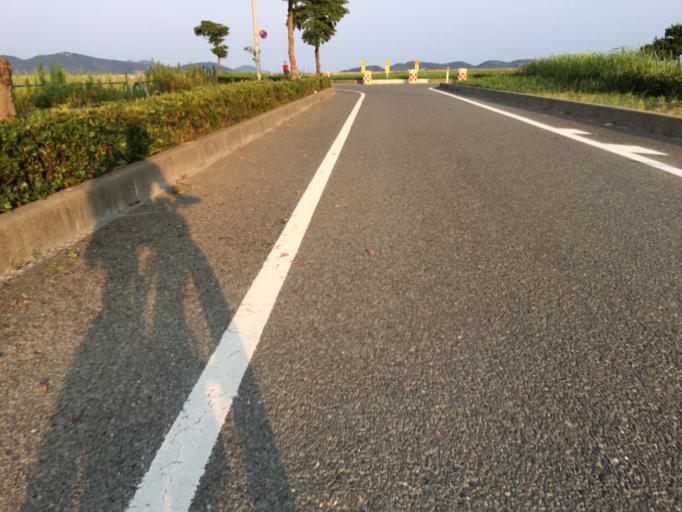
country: JP
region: Yamaguchi
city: Ogori-shimogo
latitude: 34.0076
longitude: 131.3764
